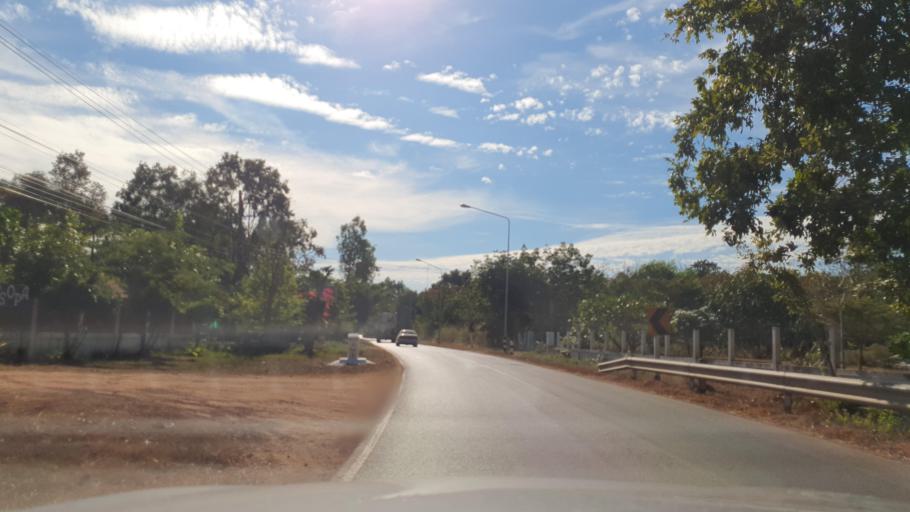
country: TH
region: Kalasin
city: Kuchinarai
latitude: 16.5403
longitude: 104.0805
